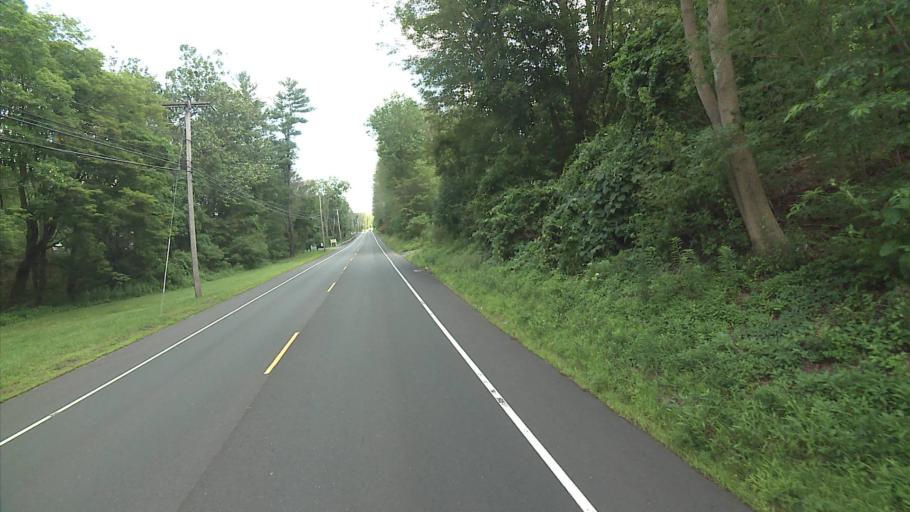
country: US
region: Connecticut
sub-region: Middlesex County
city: Higganum
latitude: 41.5055
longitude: -72.5776
